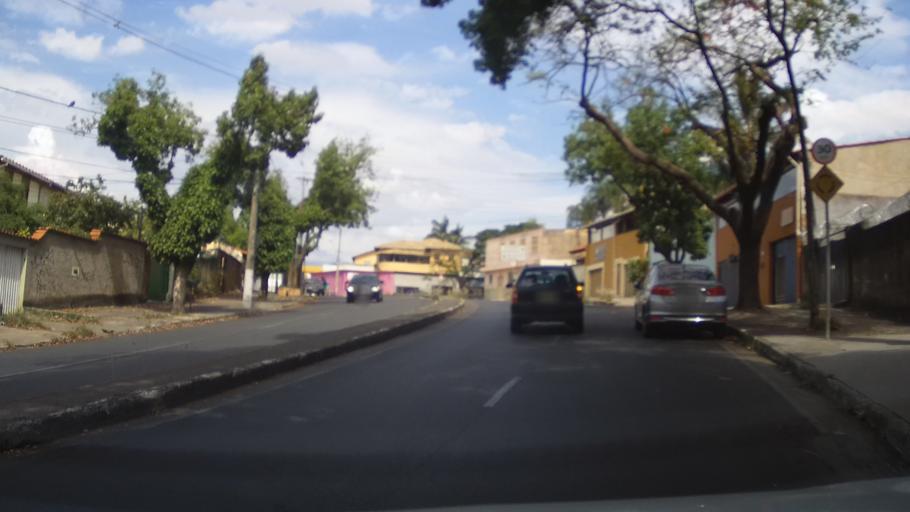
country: BR
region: Minas Gerais
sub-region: Belo Horizonte
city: Belo Horizonte
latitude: -19.8328
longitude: -43.9747
